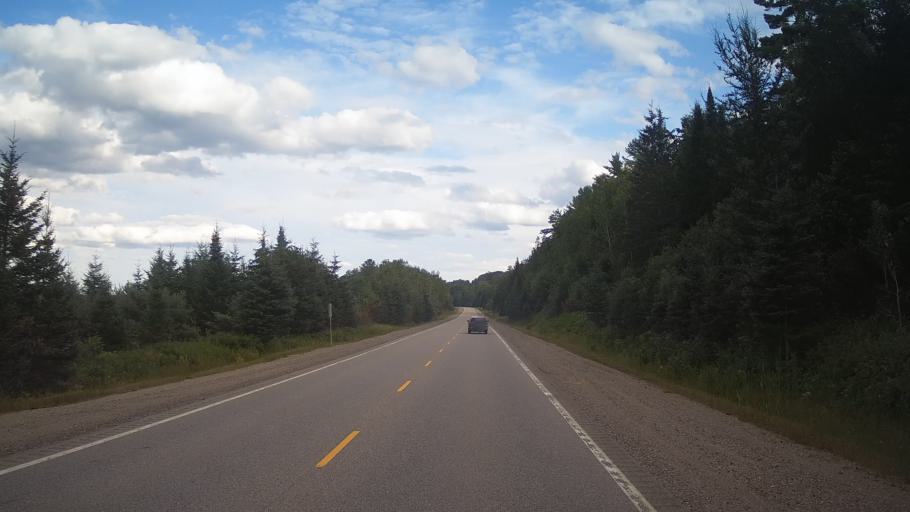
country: CA
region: Ontario
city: Mattawa
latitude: 46.2618
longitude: -78.3456
